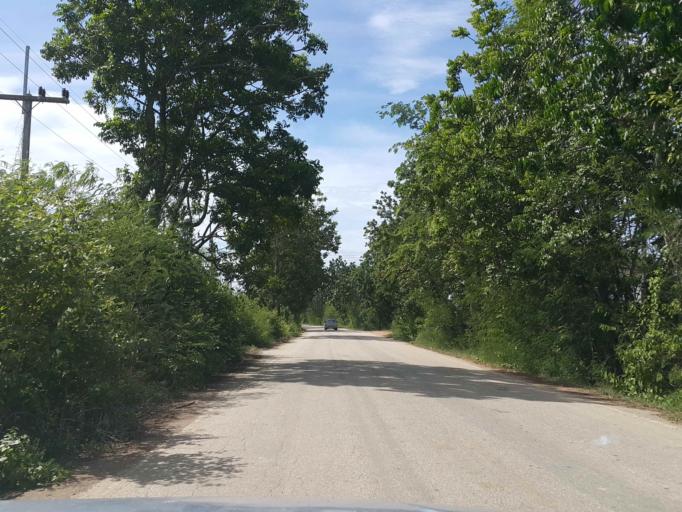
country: TH
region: Sukhothai
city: Ban Dan Lan Hoi
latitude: 17.1426
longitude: 99.5233
